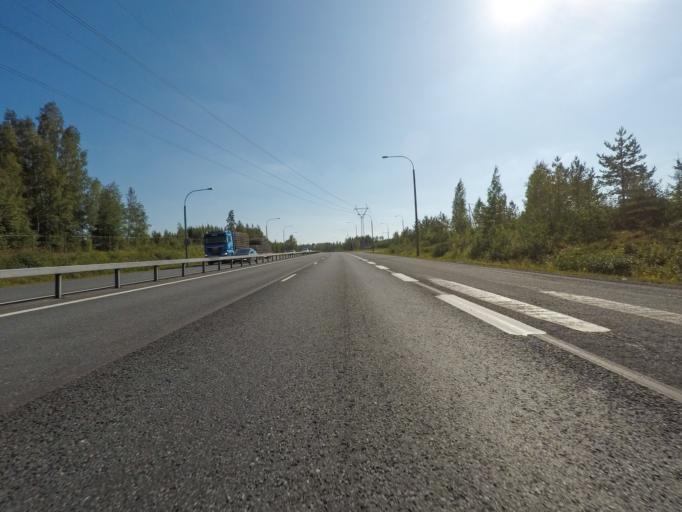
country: FI
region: Northern Savo
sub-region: Kuopio
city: Kuopio
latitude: 62.6993
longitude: 27.5669
